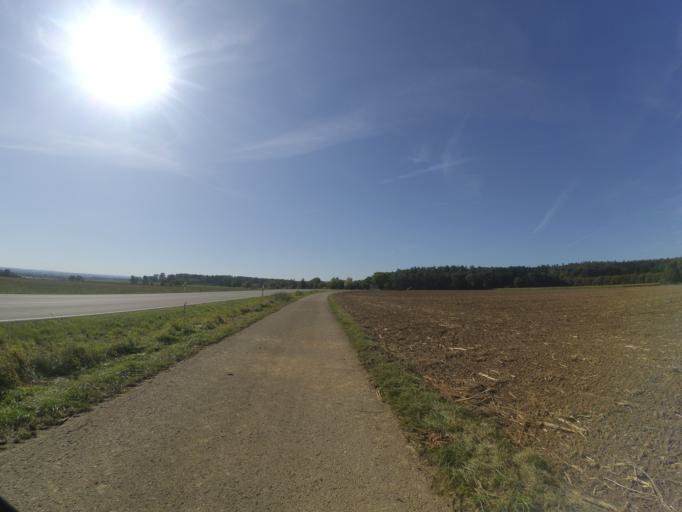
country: DE
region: Baden-Wuerttemberg
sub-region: Tuebingen Region
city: Nerenstetten
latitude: 48.5193
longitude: 10.0891
